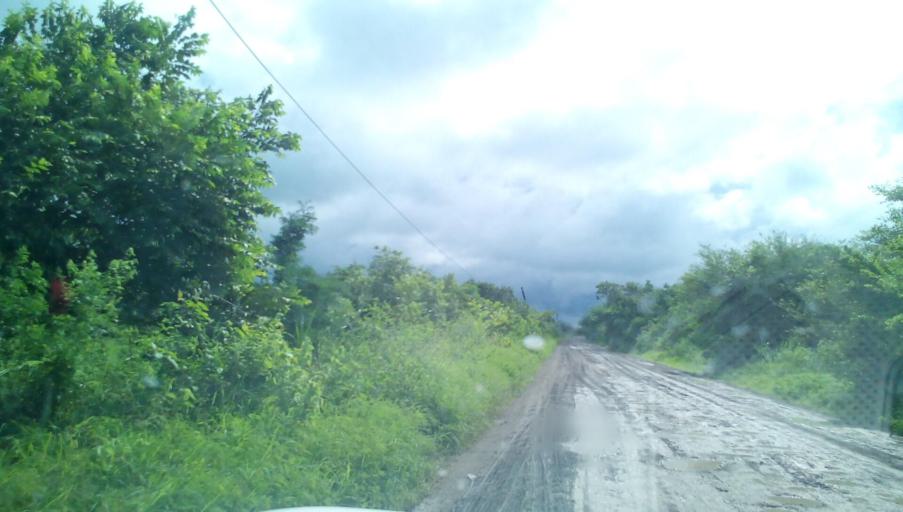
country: MX
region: Veracruz
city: Panuco
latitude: 21.8504
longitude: -98.1586
